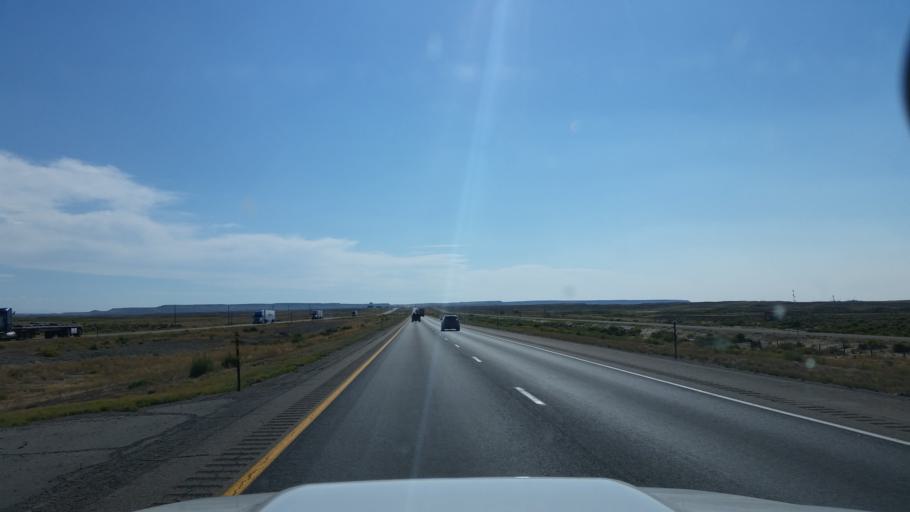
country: US
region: Wyoming
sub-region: Uinta County
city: Lyman
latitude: 41.5349
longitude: -109.9350
